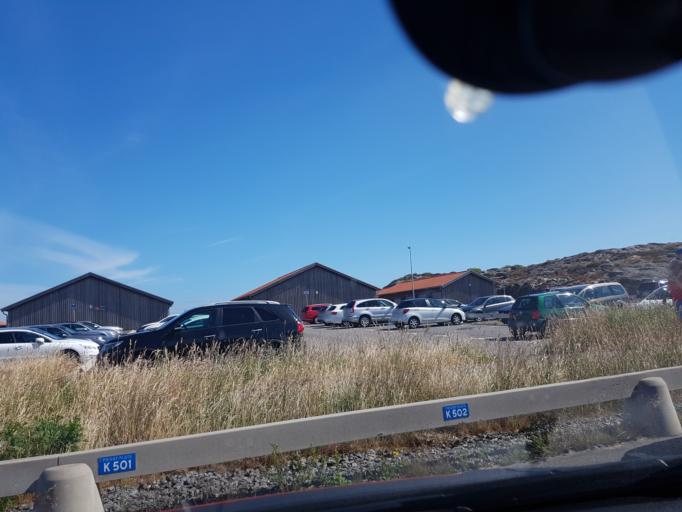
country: SE
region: Vaestra Goetaland
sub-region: Lysekils Kommun
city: Lysekil
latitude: 58.1742
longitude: 11.4176
